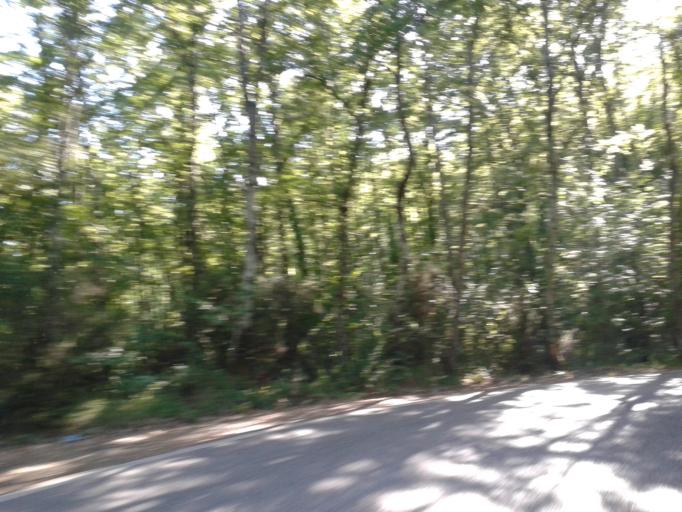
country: IT
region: Tuscany
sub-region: Province of Pisa
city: Chianni
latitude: 43.4479
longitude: 10.6237
